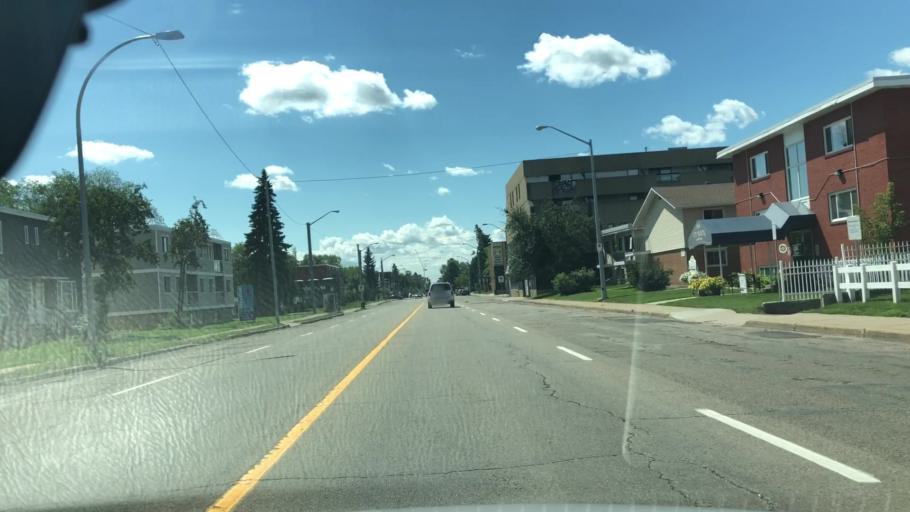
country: CA
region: Alberta
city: Edmonton
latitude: 53.5616
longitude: -113.5360
